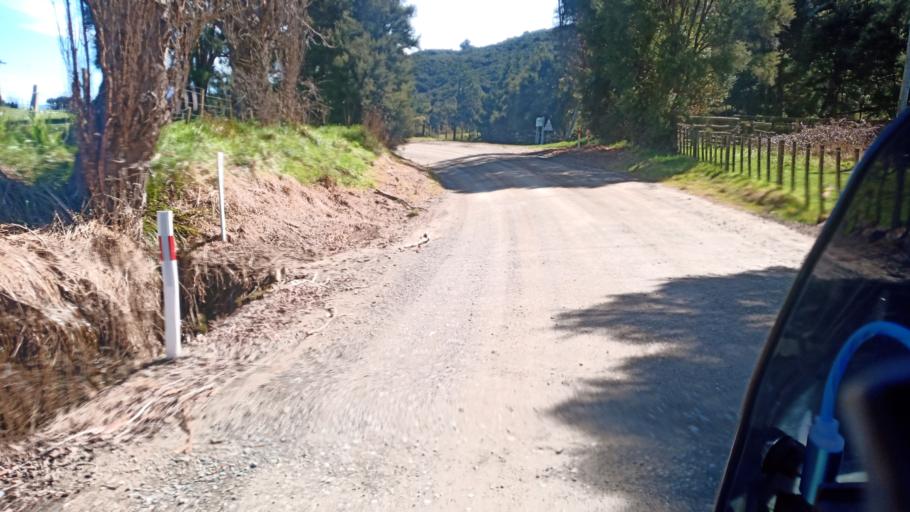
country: NZ
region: Gisborne
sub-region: Gisborne District
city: Gisborne
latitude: -37.9930
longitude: 178.3055
